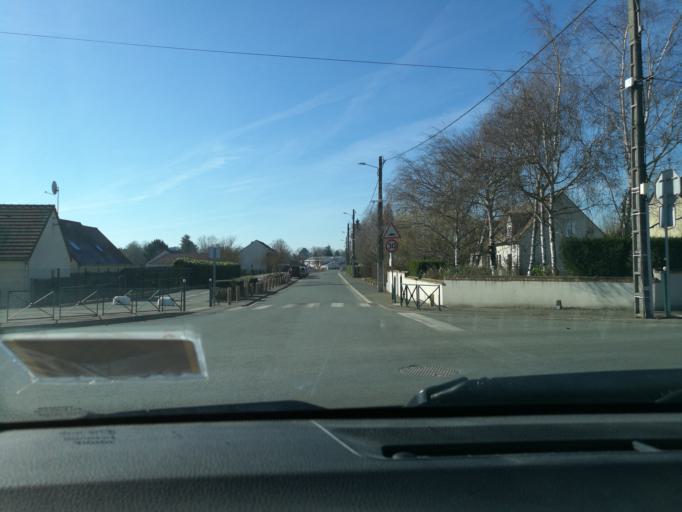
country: FR
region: Centre
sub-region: Departement du Loiret
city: Saint-Ay
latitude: 47.8635
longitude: 1.7580
